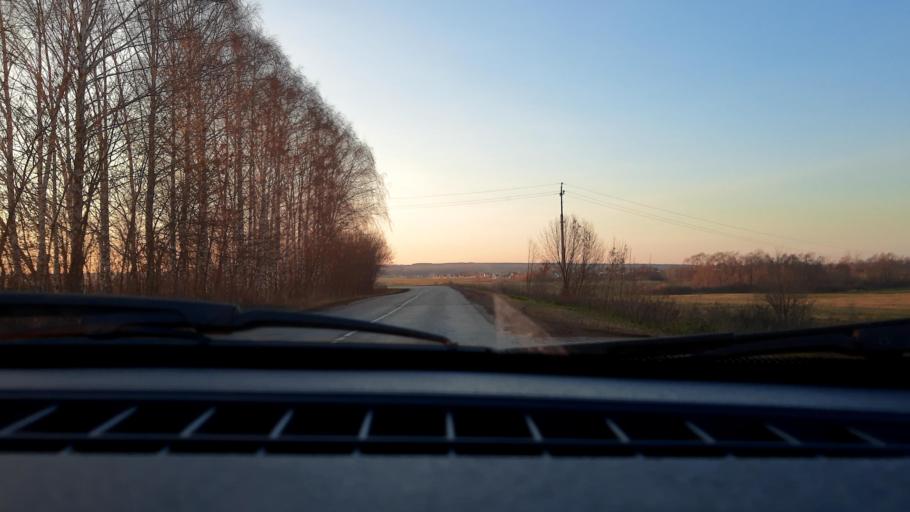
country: RU
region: Bashkortostan
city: Mikhaylovka
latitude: 54.8279
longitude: 55.9723
